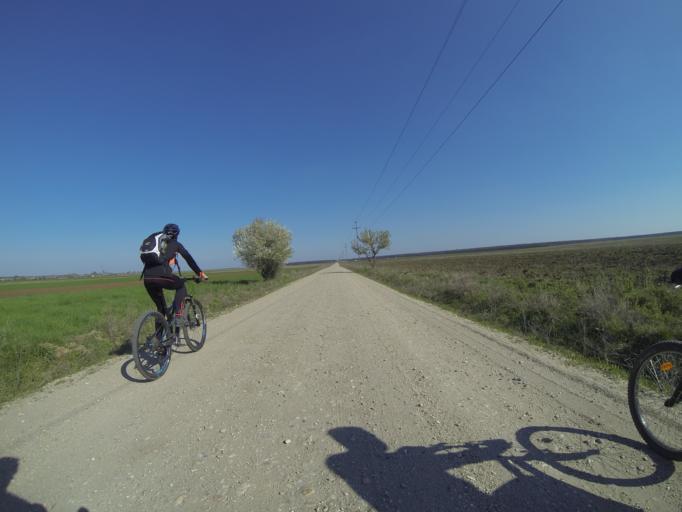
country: RO
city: Varvoru
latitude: 44.2211
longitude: 23.6412
